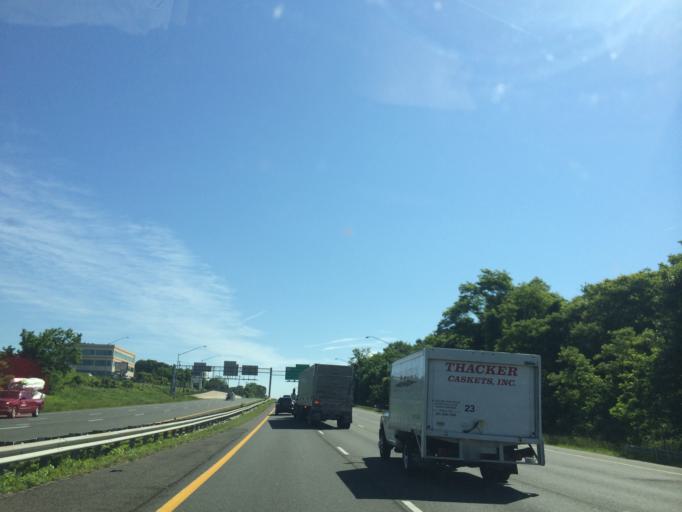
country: US
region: Maryland
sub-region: Anne Arundel County
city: Arnold
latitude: 39.0215
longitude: -76.4756
